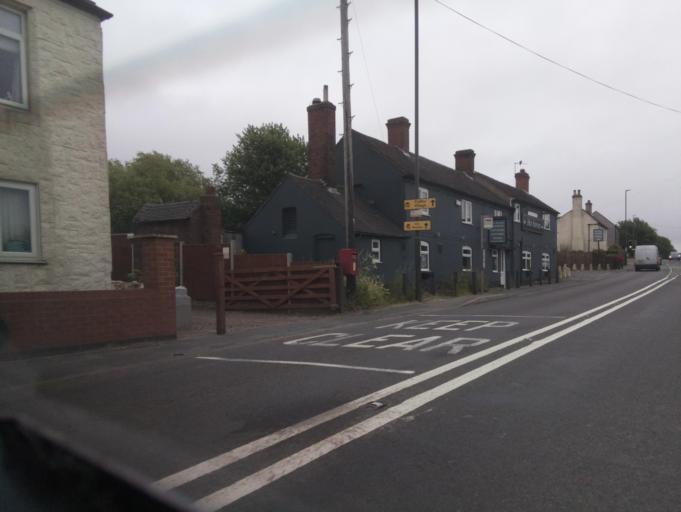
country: GB
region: England
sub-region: Derbyshire
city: Swadlincote
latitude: 52.7758
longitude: -1.6018
